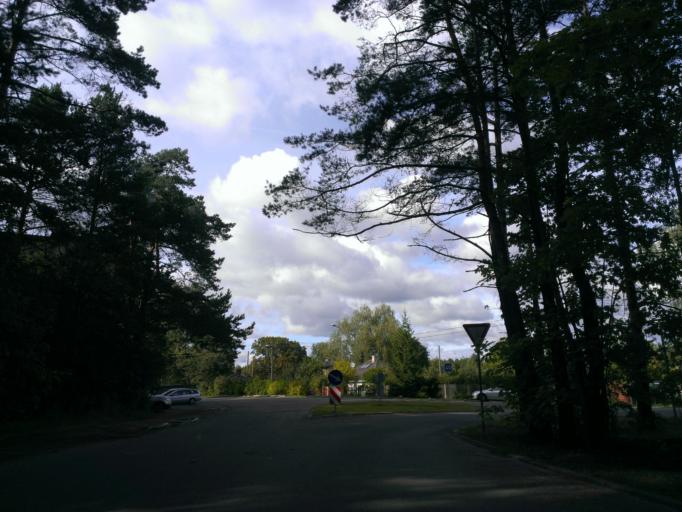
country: LV
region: Riga
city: Bergi
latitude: 56.9904
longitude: 24.2909
